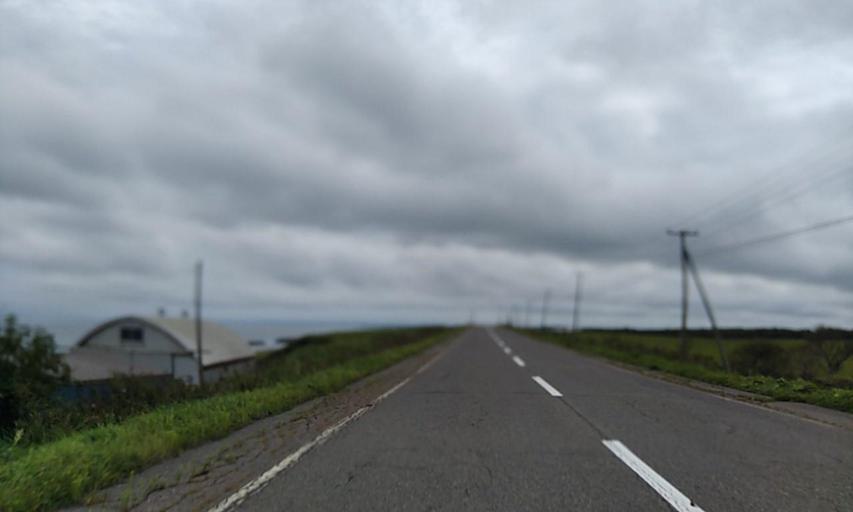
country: JP
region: Hokkaido
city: Shibetsu
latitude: 43.4226
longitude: 145.2674
